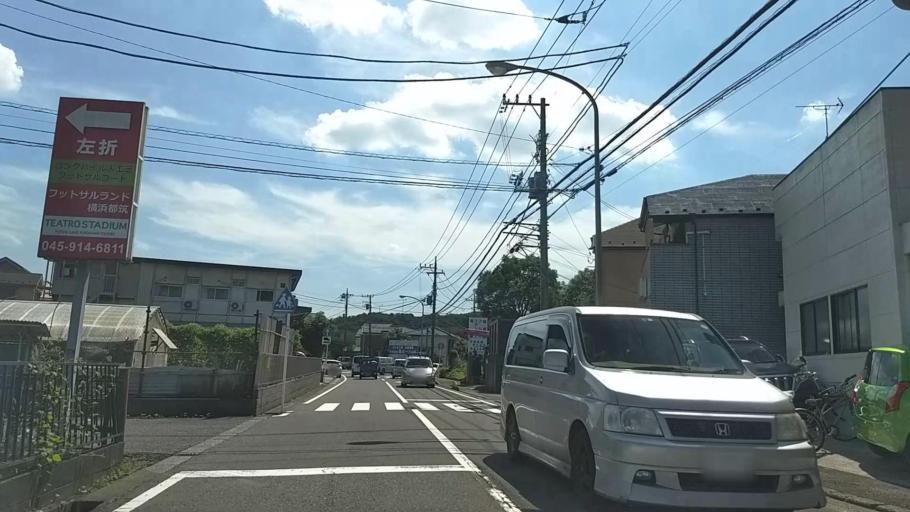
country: JP
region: Tokyo
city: Chofugaoka
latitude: 35.5550
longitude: 139.5669
